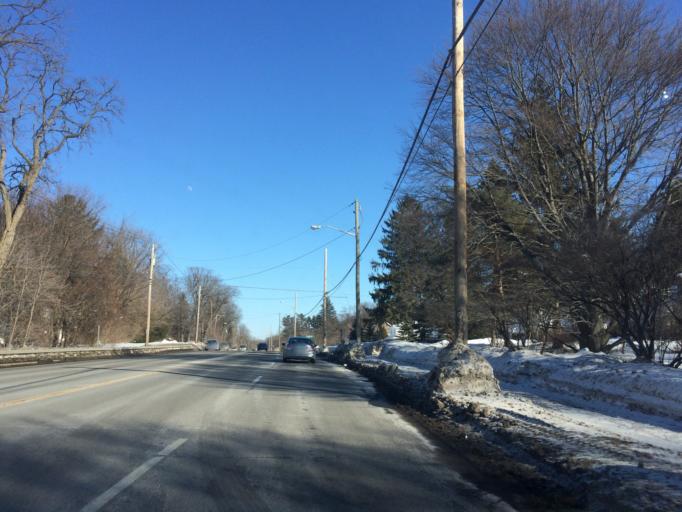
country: US
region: New York
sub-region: Monroe County
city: East Rochester
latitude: 43.1022
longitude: -77.4776
